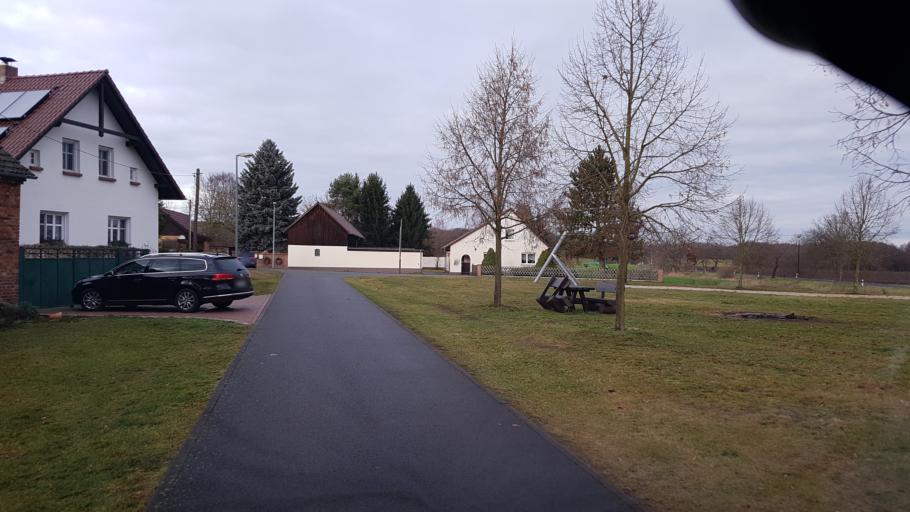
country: DE
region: Brandenburg
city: Altdobern
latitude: 51.6544
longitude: 13.9969
